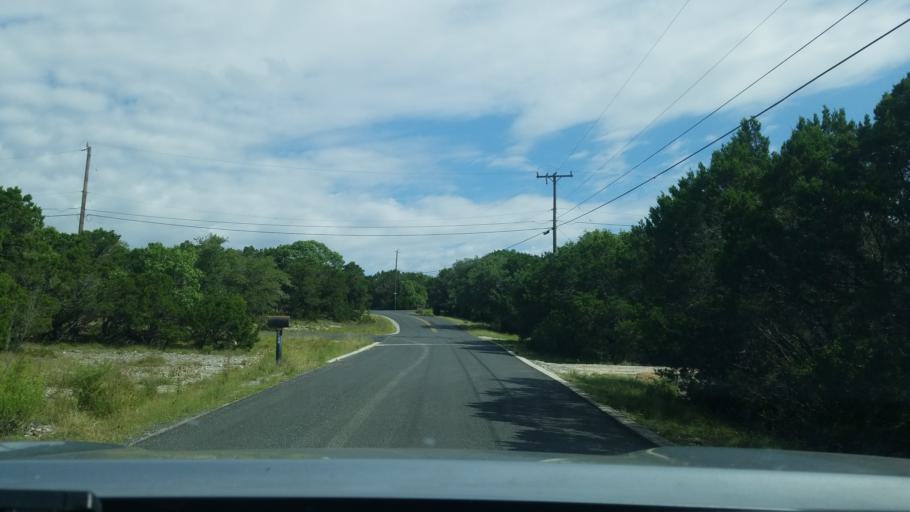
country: US
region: Texas
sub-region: Comal County
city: Bulverde
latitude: 29.7665
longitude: -98.4463
